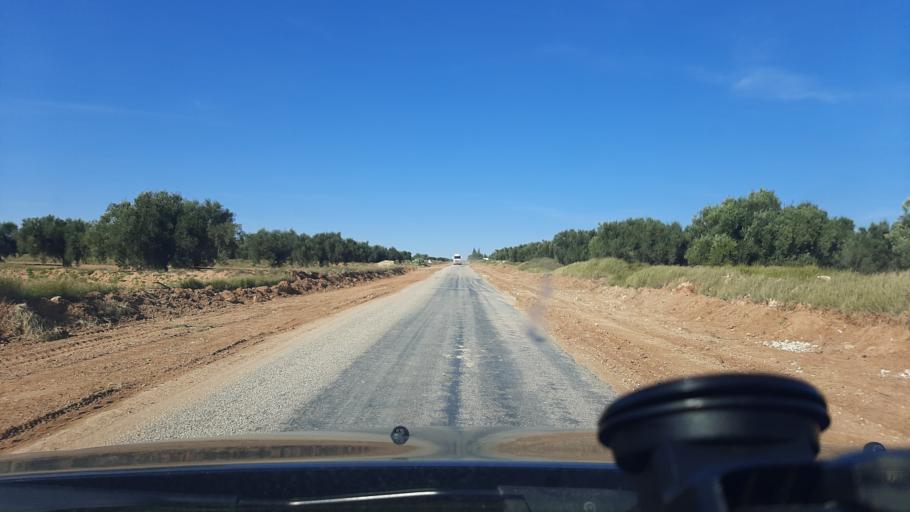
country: TN
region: Safaqis
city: Sfax
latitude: 34.9373
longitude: 10.5615
